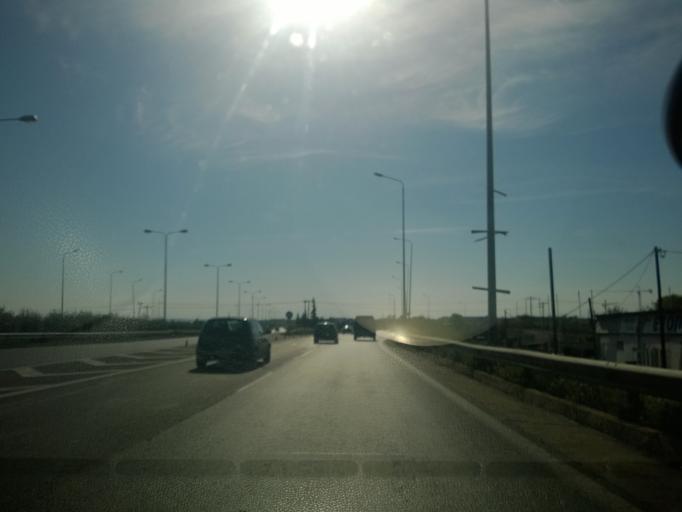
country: GR
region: Central Macedonia
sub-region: Nomos Thessalonikis
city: Pylaia
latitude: 40.5836
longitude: 22.9795
